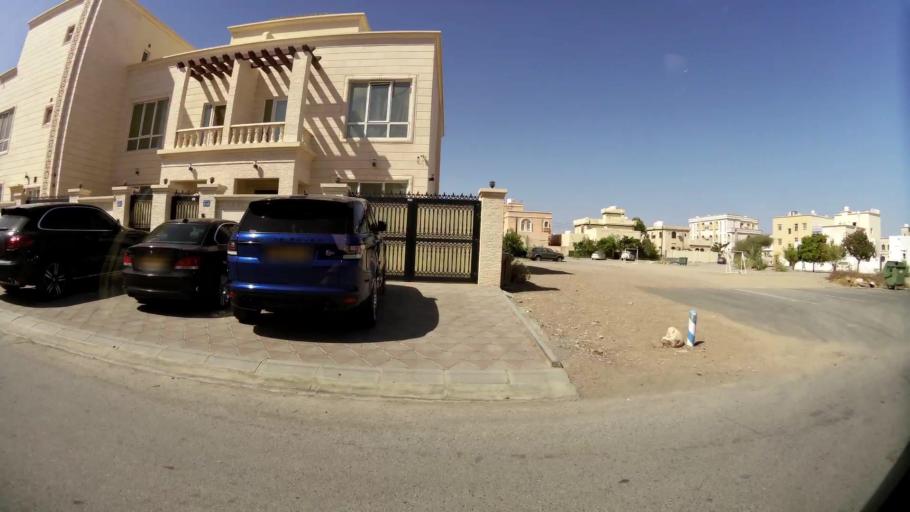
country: OM
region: Muhafazat Masqat
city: As Sib al Jadidah
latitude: 23.6088
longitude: 58.2415
